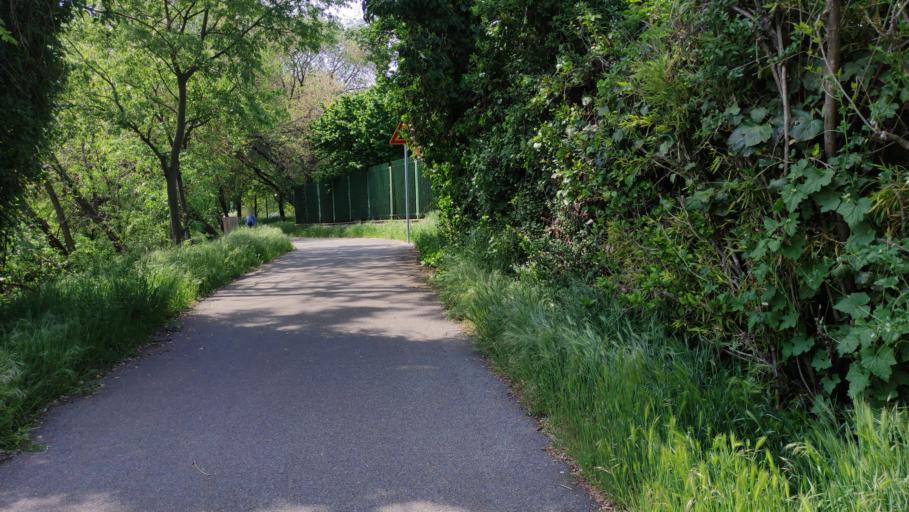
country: IT
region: Piedmont
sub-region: Provincia di Torino
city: Nichelino
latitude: 45.0082
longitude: 7.6511
